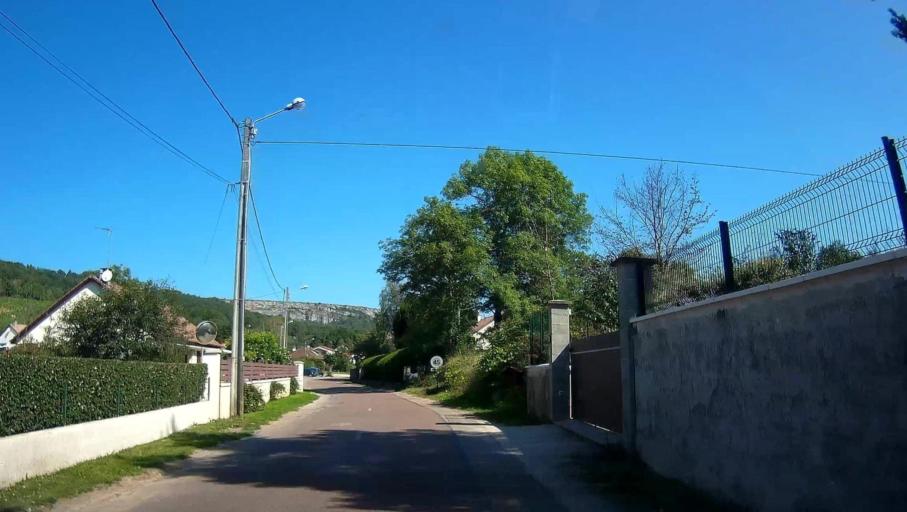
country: FR
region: Bourgogne
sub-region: Departement de la Cote-d'Or
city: Nolay
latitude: 46.9638
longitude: 4.6434
